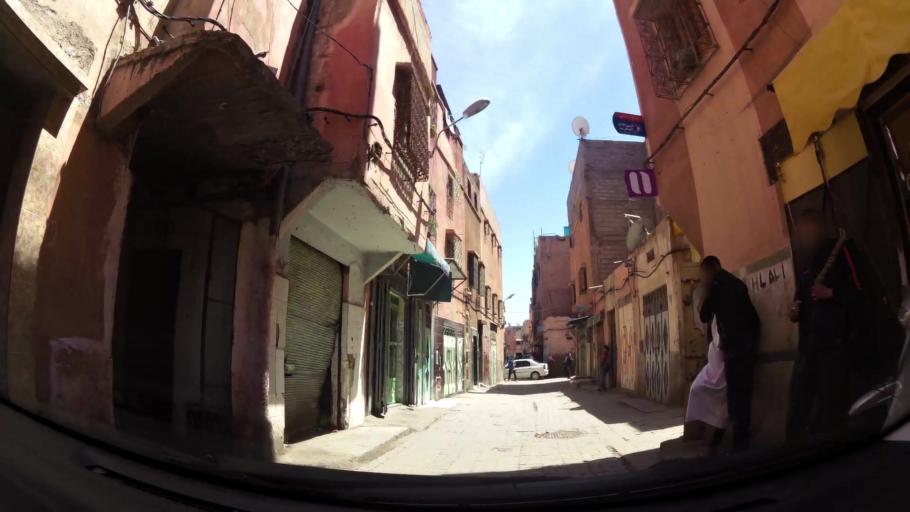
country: MA
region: Marrakech-Tensift-Al Haouz
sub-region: Marrakech
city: Marrakesh
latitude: 31.6193
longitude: -7.9678
